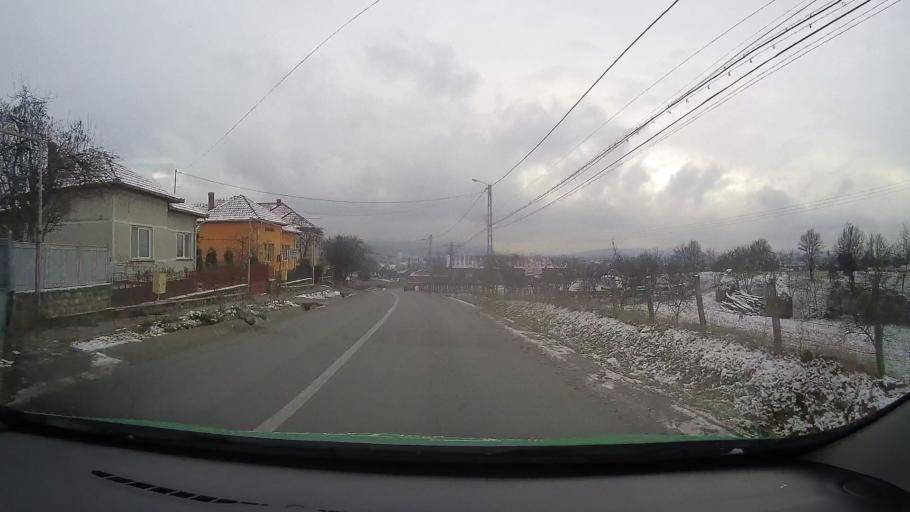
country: RO
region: Hunedoara
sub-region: Oras Hateg
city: Hateg
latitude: 45.6170
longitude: 22.9433
